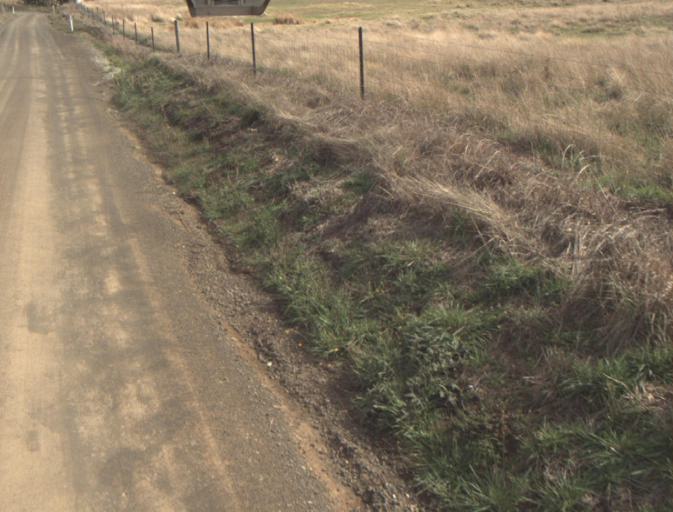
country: AU
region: Tasmania
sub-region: Launceston
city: Mayfield
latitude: -41.1907
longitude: 147.1900
